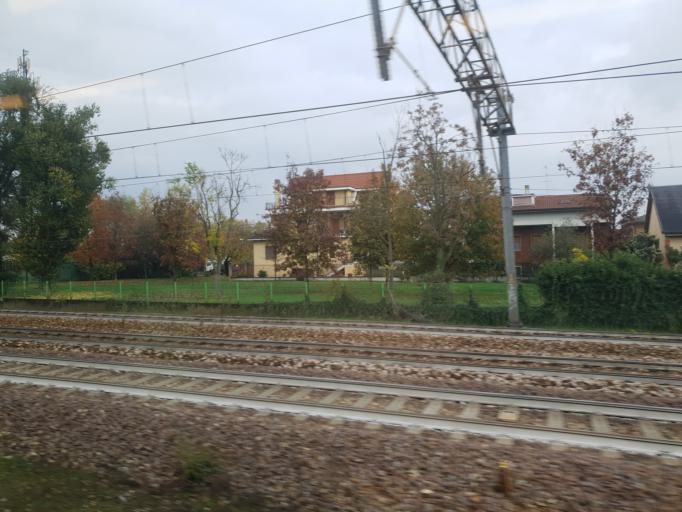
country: IT
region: Lombardy
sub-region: Citta metropolitana di Milano
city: Novate Milanese
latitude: 45.5161
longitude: 9.1479
